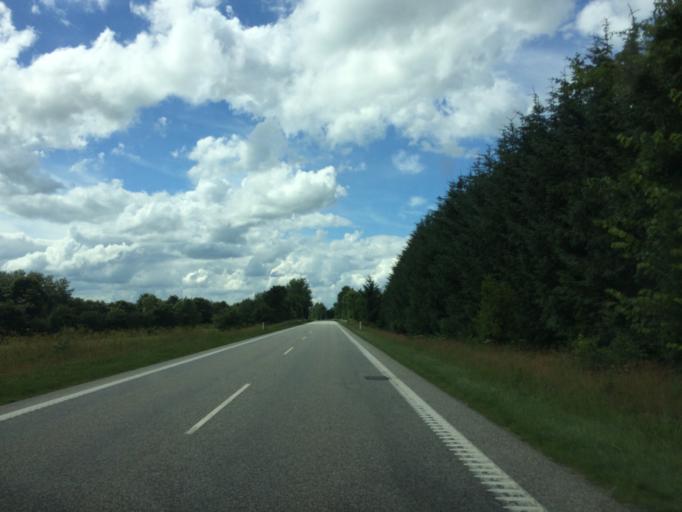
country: DK
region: North Denmark
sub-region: Vesthimmerland Kommune
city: Alestrup
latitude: 56.6223
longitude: 9.5570
